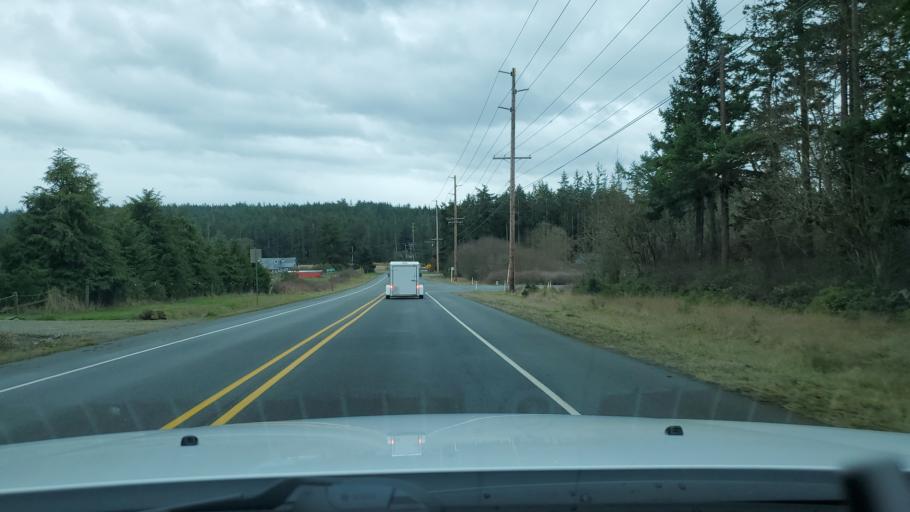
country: US
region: Washington
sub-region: Island County
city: Coupeville
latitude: 48.2345
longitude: -122.7518
